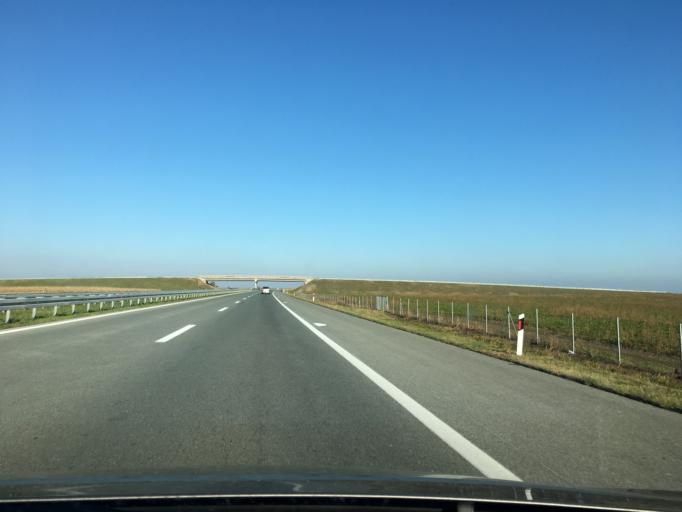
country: RS
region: Autonomna Pokrajina Vojvodina
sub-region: Severnobacki Okrug
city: Mali Igos
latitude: 45.7293
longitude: 19.7059
